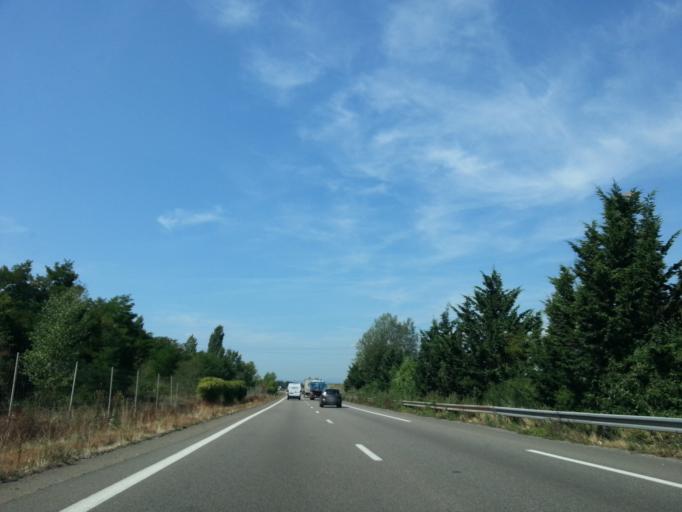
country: FR
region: Alsace
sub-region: Departement du Bas-Rhin
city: Lingolsheim
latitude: 48.5271
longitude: 7.6816
